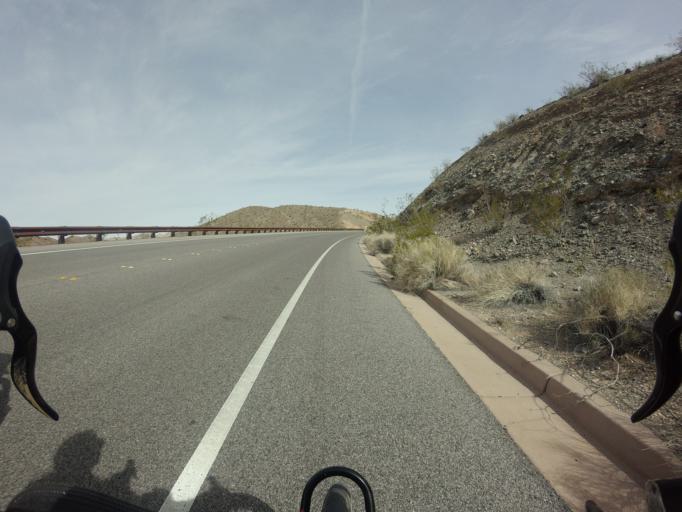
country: US
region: Nevada
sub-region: Clark County
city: Boulder City
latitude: 36.1623
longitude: -114.7878
